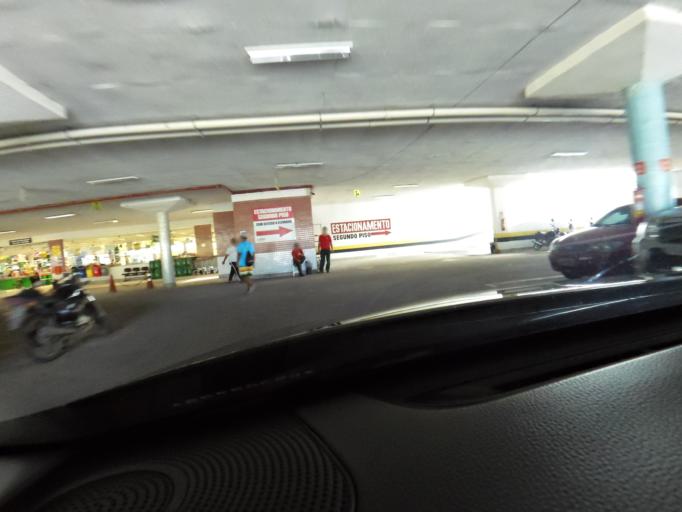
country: BR
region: Espirito Santo
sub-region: Guarapari
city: Guarapari
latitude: -20.6460
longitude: -40.4890
